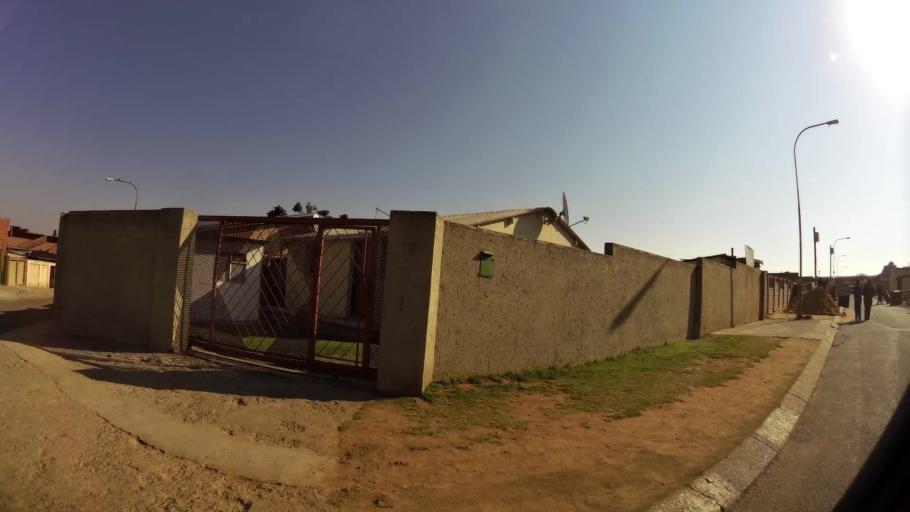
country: ZA
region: Gauteng
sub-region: City of Johannesburg Metropolitan Municipality
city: Soweto
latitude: -26.2484
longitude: 27.9502
